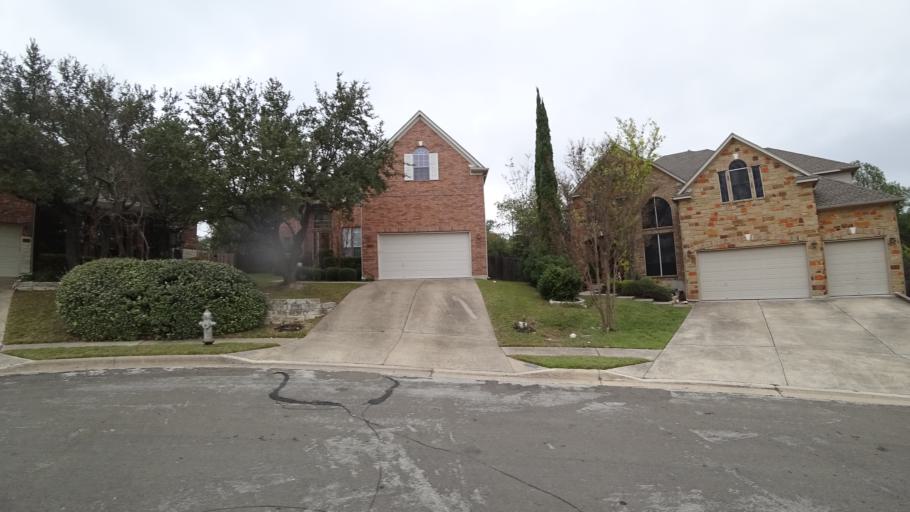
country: US
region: Texas
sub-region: Williamson County
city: Anderson Mill
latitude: 30.4344
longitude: -97.8251
